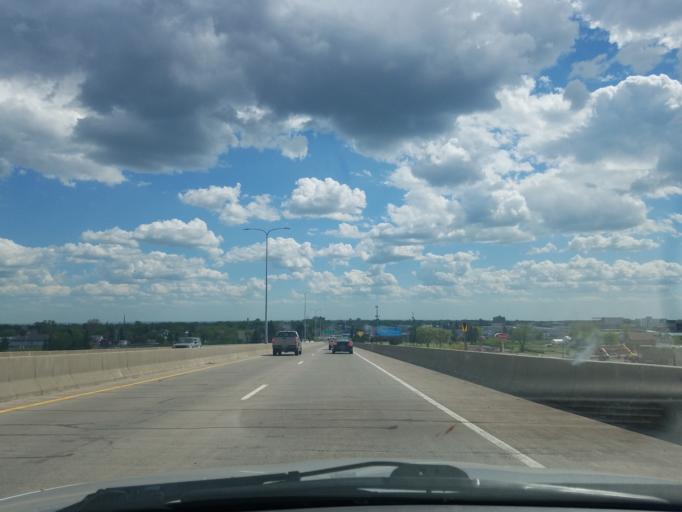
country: US
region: Wisconsin
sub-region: Douglas County
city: Superior
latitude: 46.7379
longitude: -92.0980
